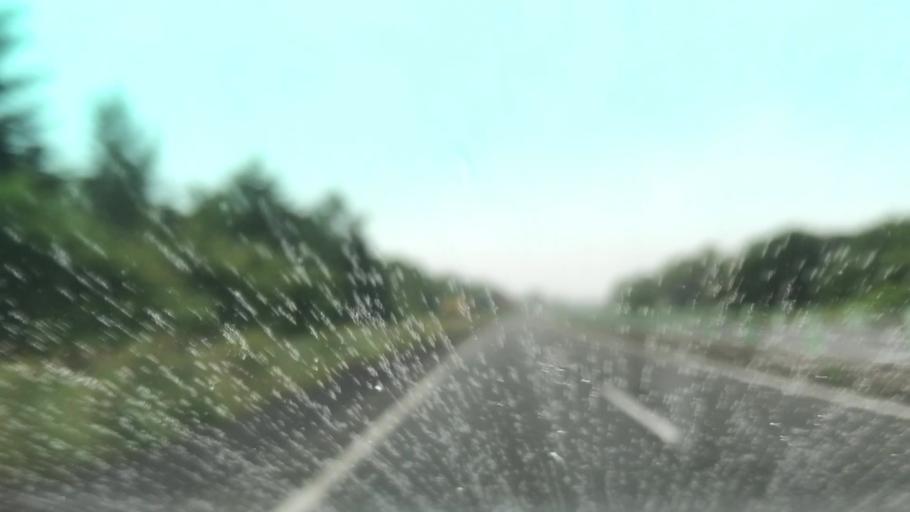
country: JP
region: Hokkaido
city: Shiraoi
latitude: 42.5145
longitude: 141.2699
